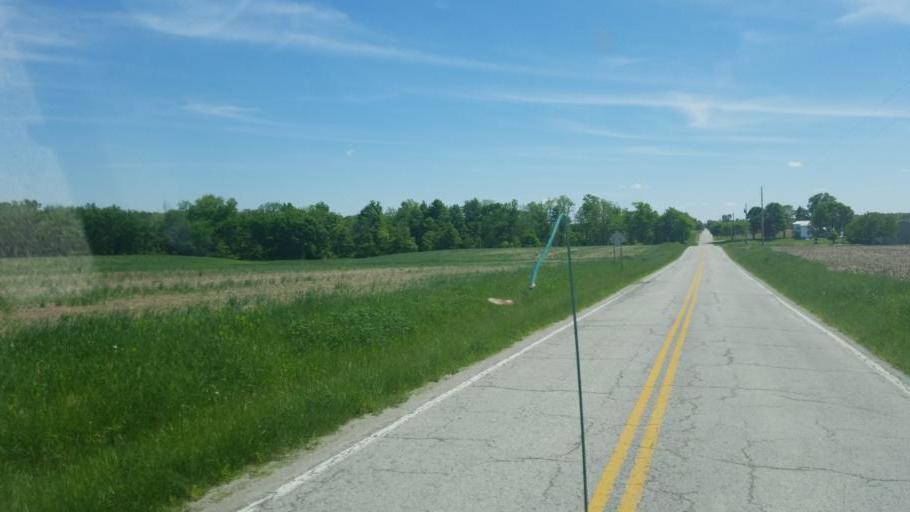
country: US
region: Ohio
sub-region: Huron County
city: Willard
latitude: 41.1042
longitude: -82.7542
